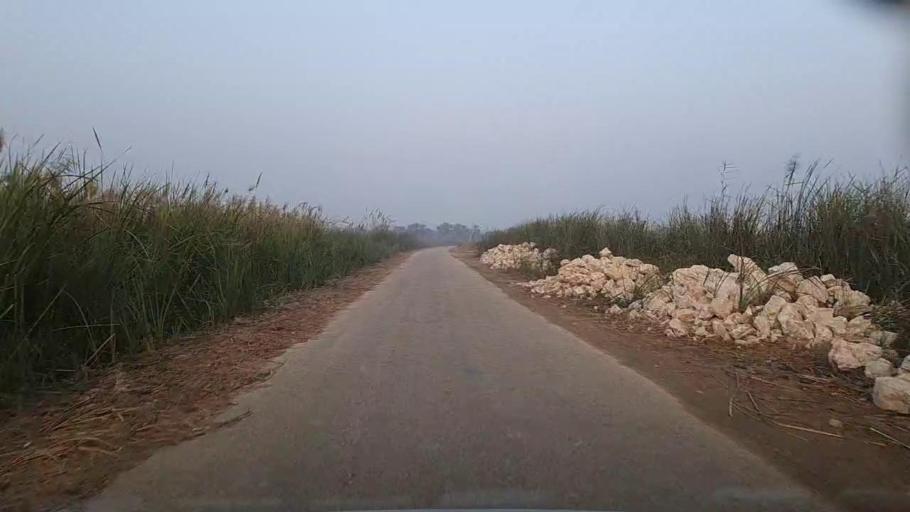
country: PK
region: Sindh
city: Kandiari
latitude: 27.0389
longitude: 68.5789
